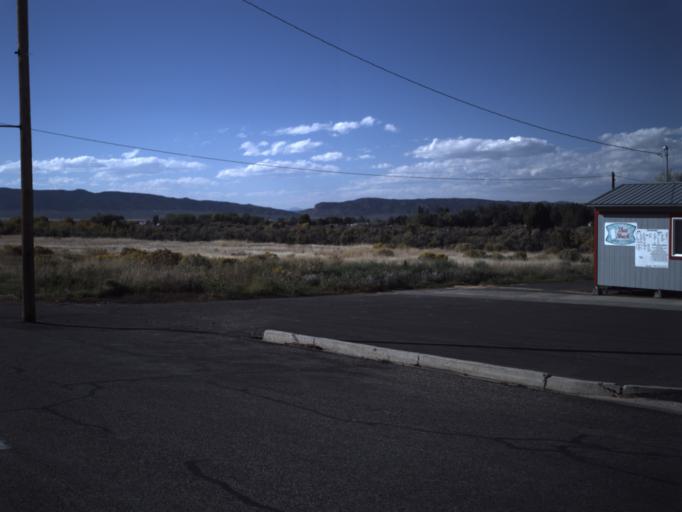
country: US
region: Utah
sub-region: Iron County
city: Parowan
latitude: 37.8388
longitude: -112.8417
